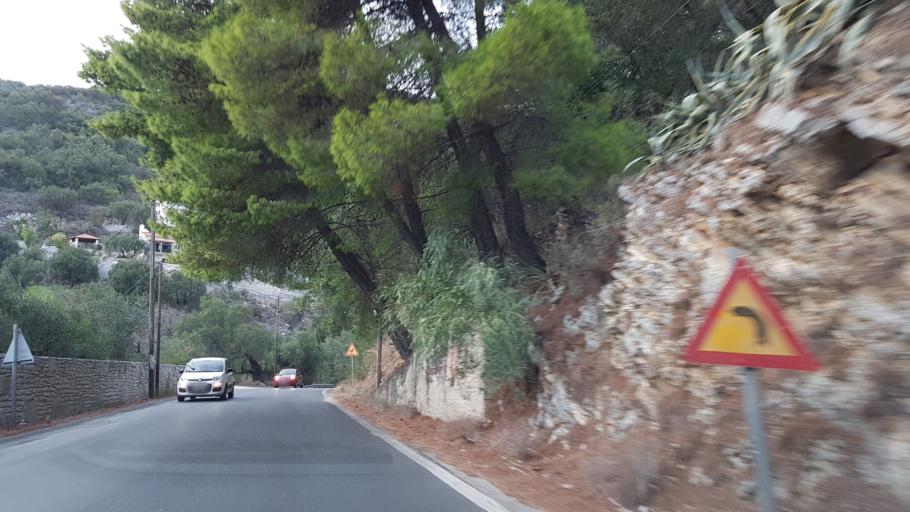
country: GR
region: Ionian Islands
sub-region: Nomos Kerkyras
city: Kontokali
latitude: 39.7309
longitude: 19.9131
